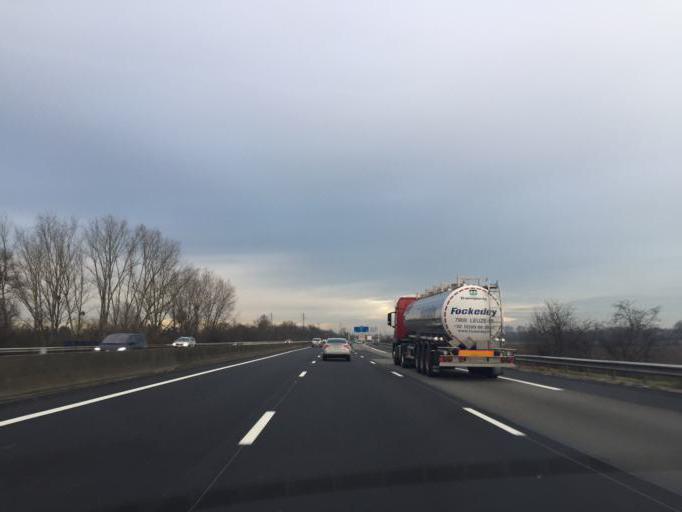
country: FR
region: Rhone-Alpes
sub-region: Departement du Rhone
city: Belleville
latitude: 46.0944
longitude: 4.7460
